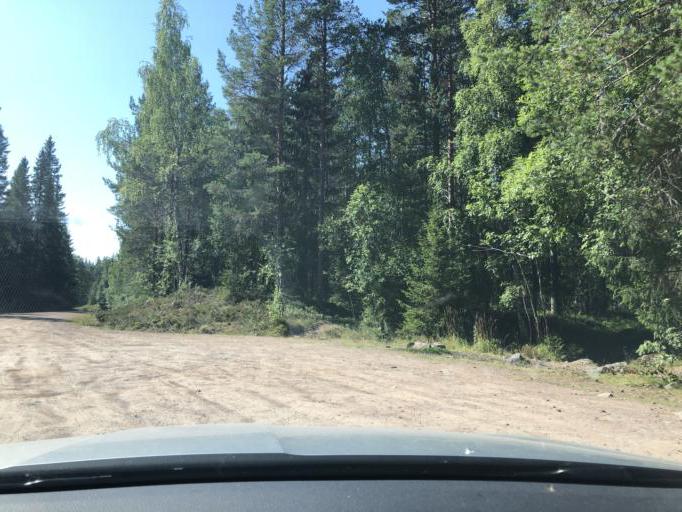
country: SE
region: Dalarna
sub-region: Orsa Kommun
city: Orsa
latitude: 61.2677
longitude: 14.7476
